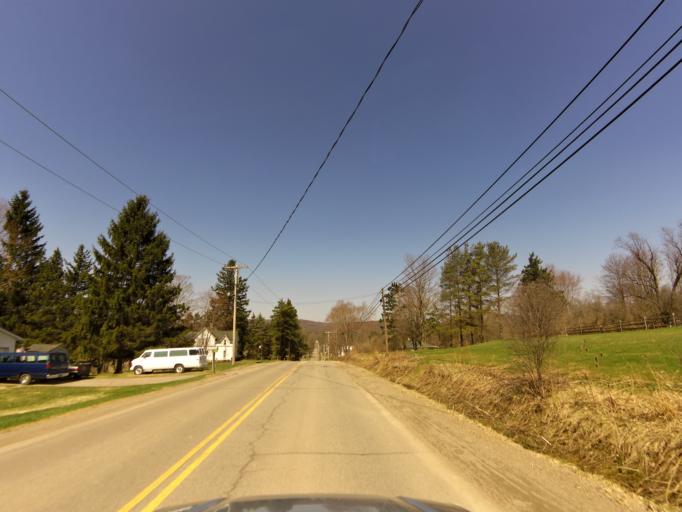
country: US
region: New York
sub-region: Cattaraugus County
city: Franklinville
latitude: 42.3323
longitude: -78.4441
